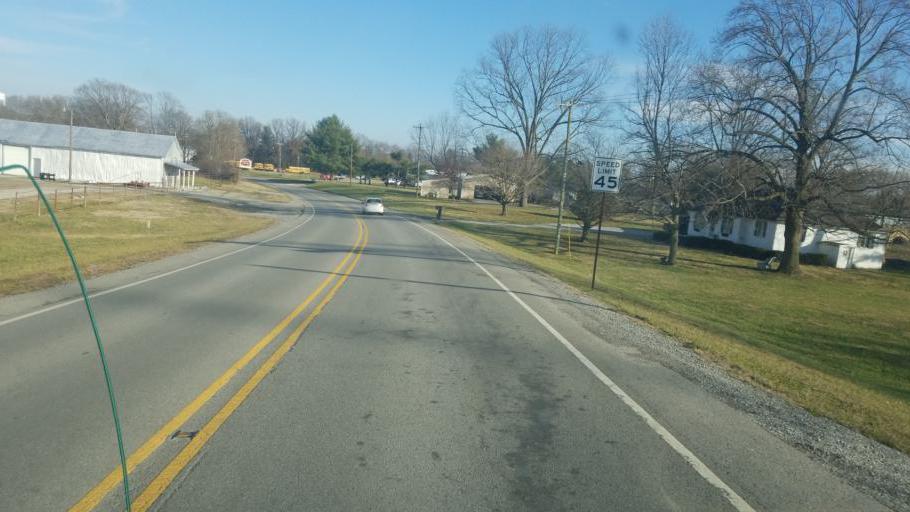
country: US
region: Illinois
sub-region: Wabash County
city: Mount Carmel
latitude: 38.4003
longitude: -87.7880
